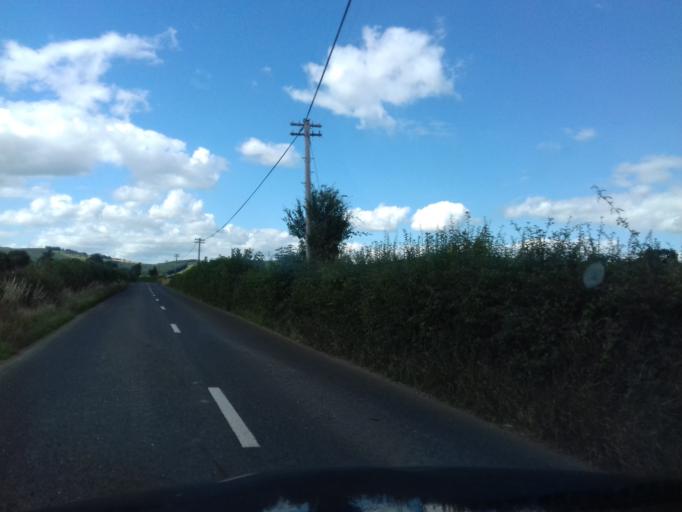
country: IE
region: Munster
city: Carrick-on-Suir
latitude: 52.3785
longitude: -7.4547
